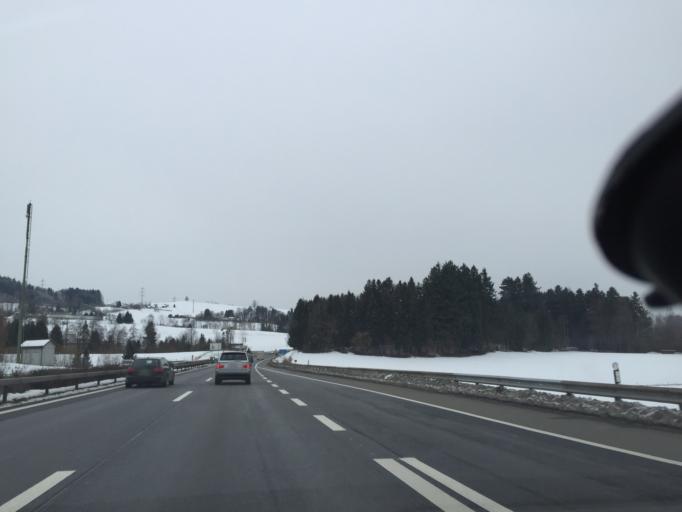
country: CH
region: Zurich
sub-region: Bezirk Horgen
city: Au / Unter-Dorf
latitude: 47.2309
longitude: 8.6289
